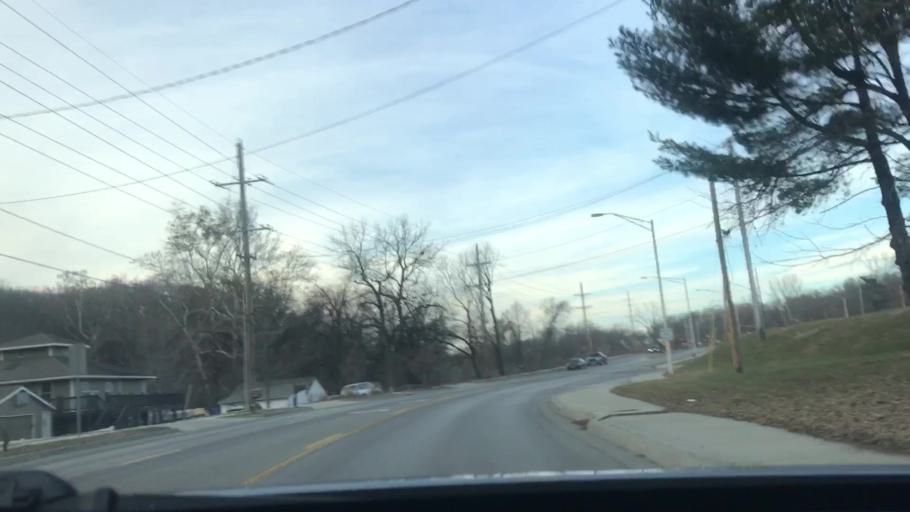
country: US
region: Missouri
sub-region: Platte County
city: Riverside
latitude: 39.2230
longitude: -94.6266
